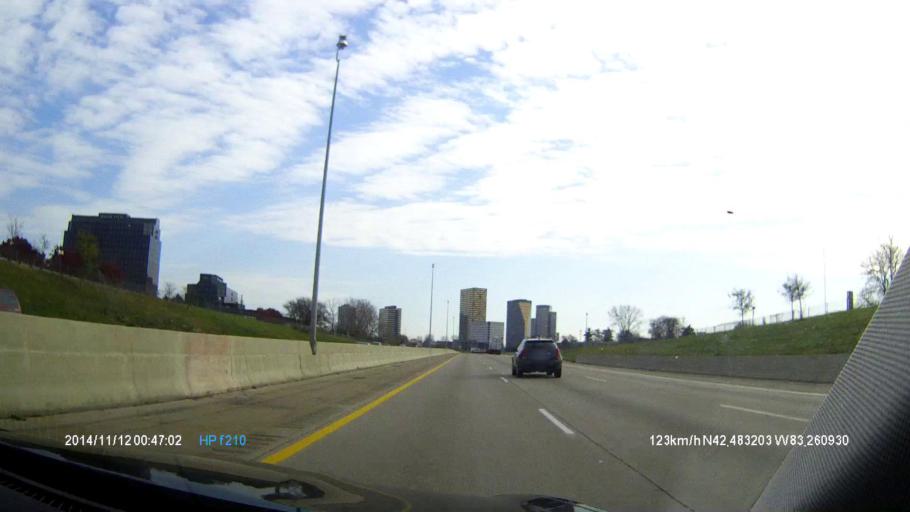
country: US
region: Michigan
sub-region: Oakland County
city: Bingham Farms
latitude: 42.4830
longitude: -83.2608
